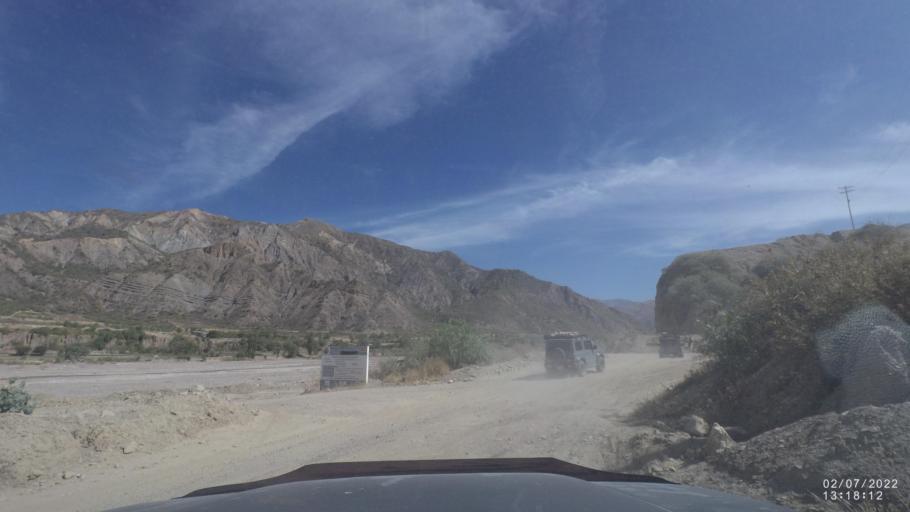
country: BO
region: Cochabamba
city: Irpa Irpa
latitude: -17.7339
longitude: -66.3122
